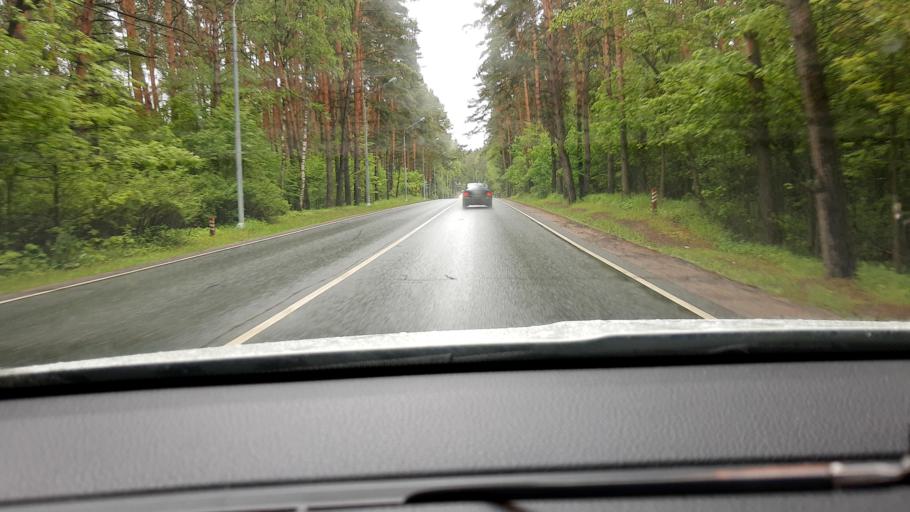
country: RU
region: Moskovskaya
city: Nikolina Gora
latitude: 55.7103
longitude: 37.0865
